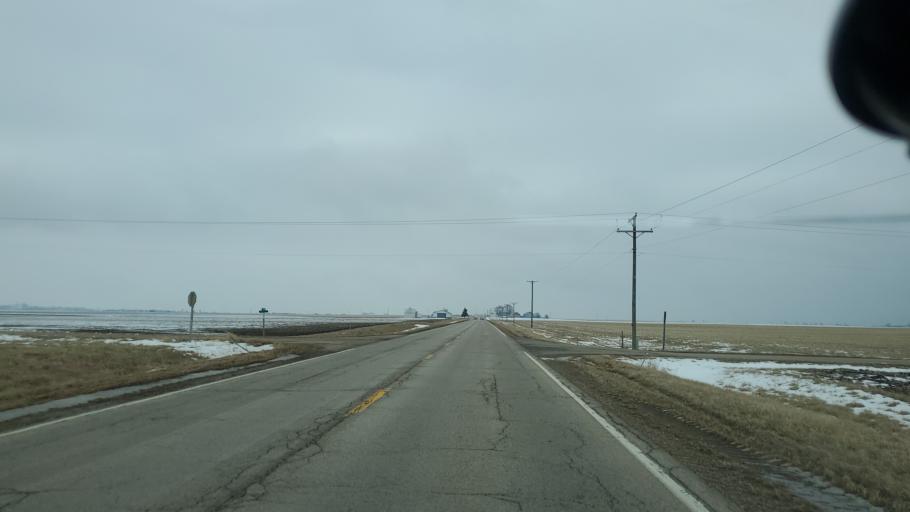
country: US
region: Illinois
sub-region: Marshall County
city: Wenona
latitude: 41.1188
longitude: -89.1054
